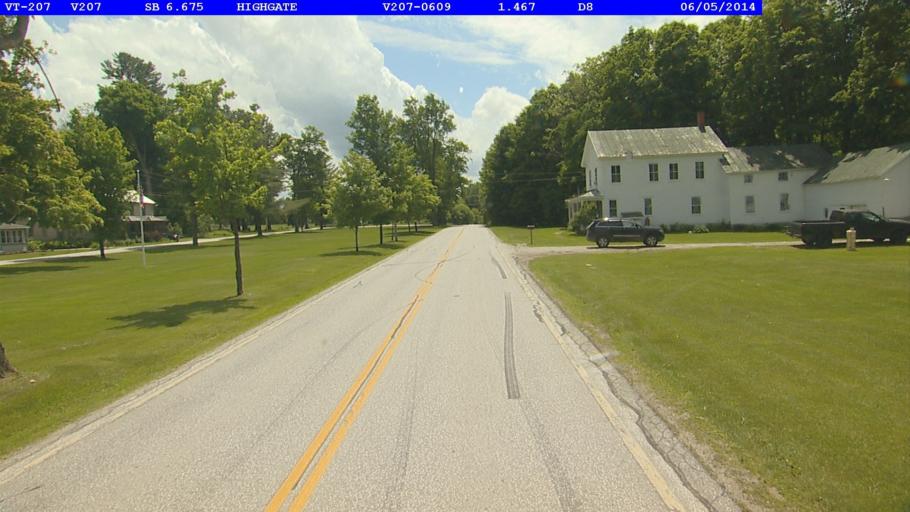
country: US
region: Vermont
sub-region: Franklin County
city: Swanton
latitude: 44.9316
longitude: -73.0489
